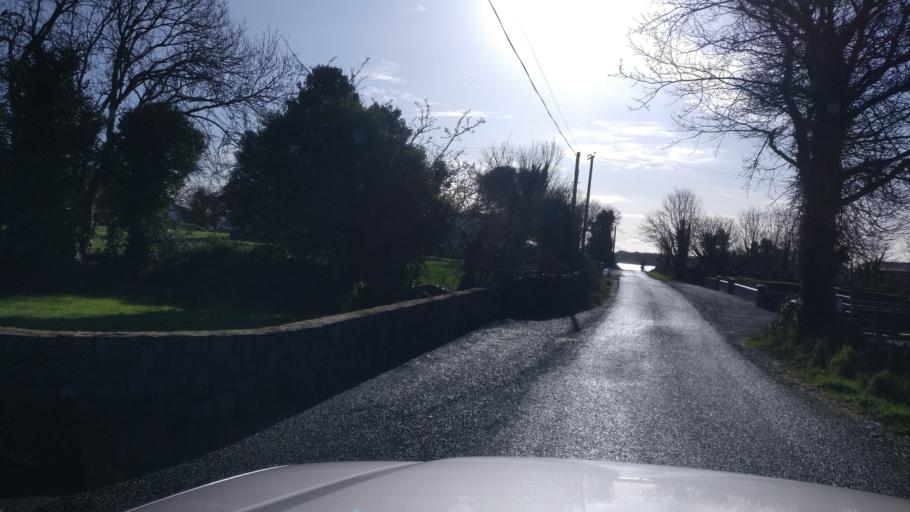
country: IE
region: Connaught
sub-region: County Galway
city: Athenry
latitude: 53.2328
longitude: -8.7790
